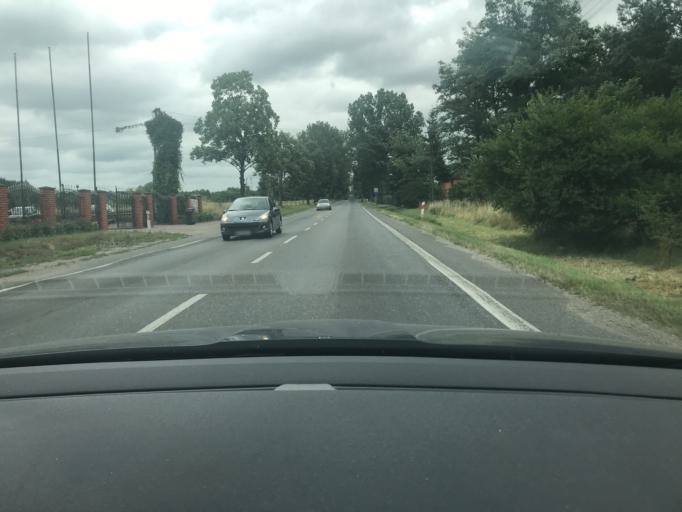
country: PL
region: Lodz Voivodeship
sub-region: Powiat poddebicki
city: Poddebice
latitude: 51.8913
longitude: 18.9713
